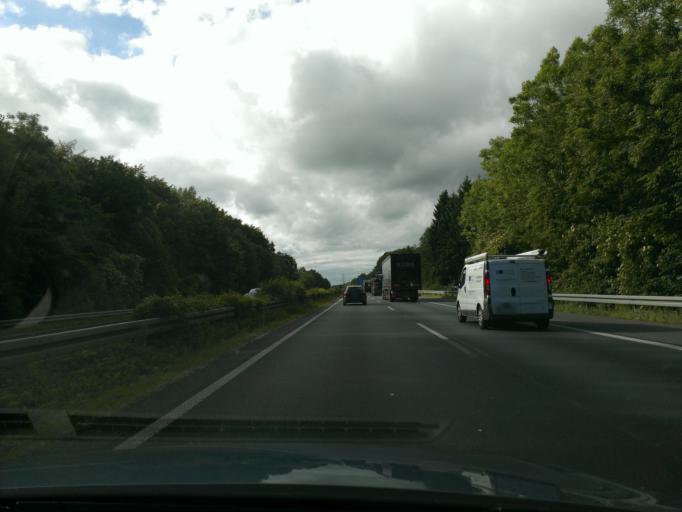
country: DE
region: North Rhine-Westphalia
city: Werne
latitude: 51.7086
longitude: 7.6599
